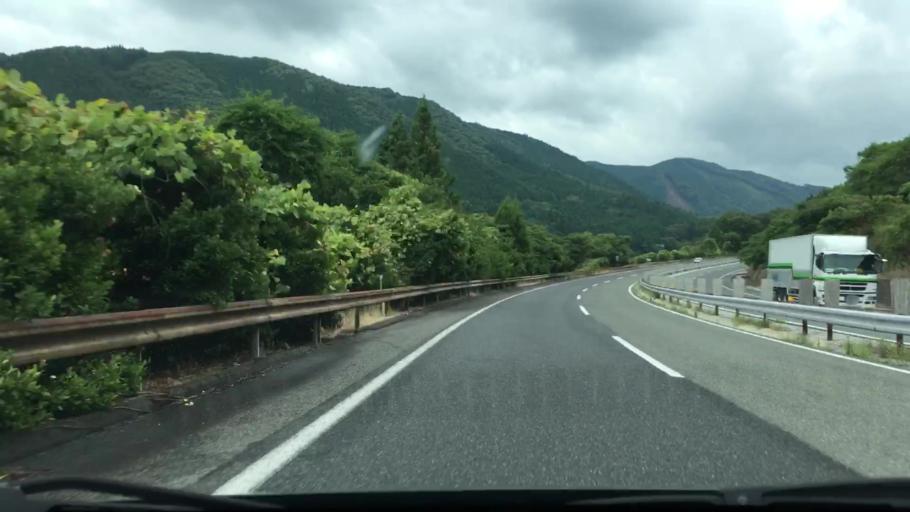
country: JP
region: Okayama
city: Niimi
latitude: 34.9849
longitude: 133.3814
